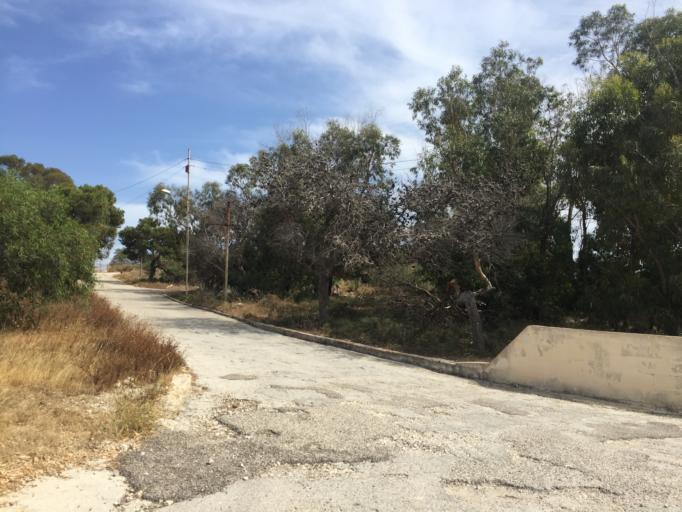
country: MT
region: Tas-Sliema
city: Sliema
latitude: 35.9045
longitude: 14.5035
